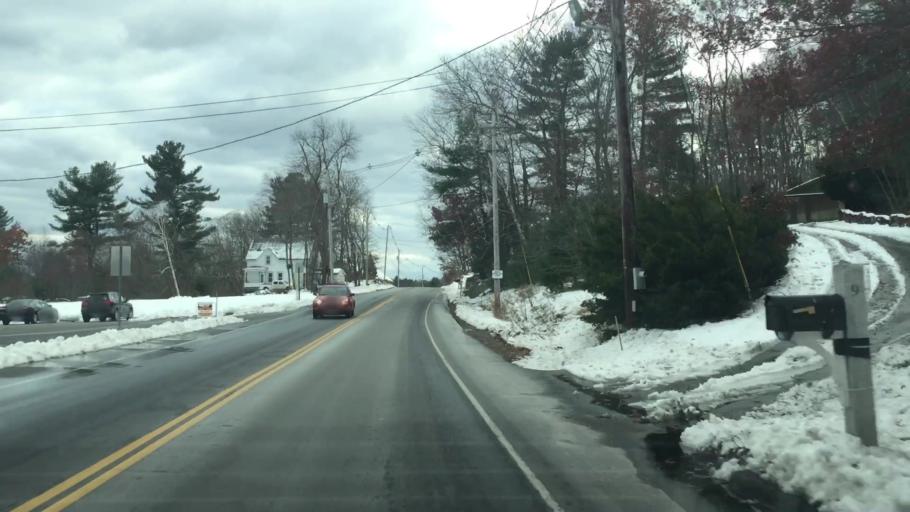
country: US
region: New Hampshire
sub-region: Hillsborough County
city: Pelham
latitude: 42.6985
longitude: -71.3521
